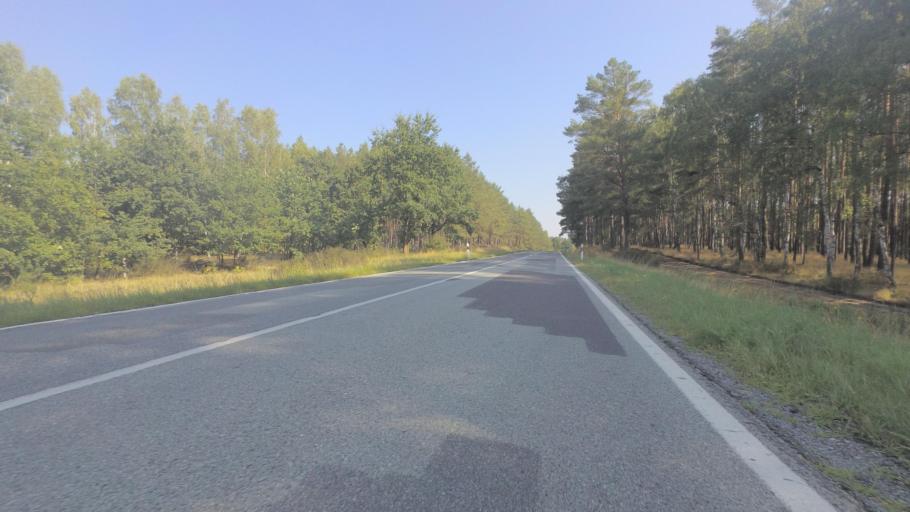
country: DE
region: Mecklenburg-Vorpommern
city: Malchow
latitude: 53.5675
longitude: 12.4536
